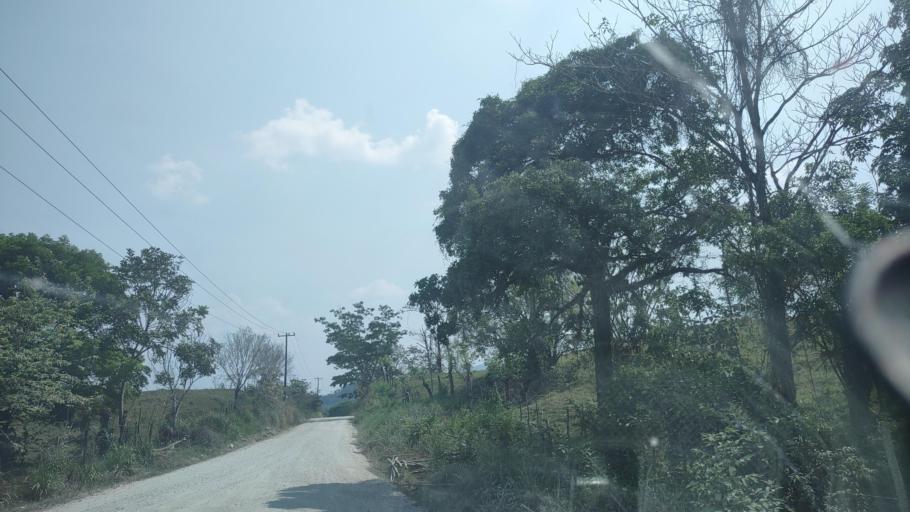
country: MX
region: Tabasco
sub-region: Huimanguillo
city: Francisco Rueda
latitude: 17.5774
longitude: -93.8884
